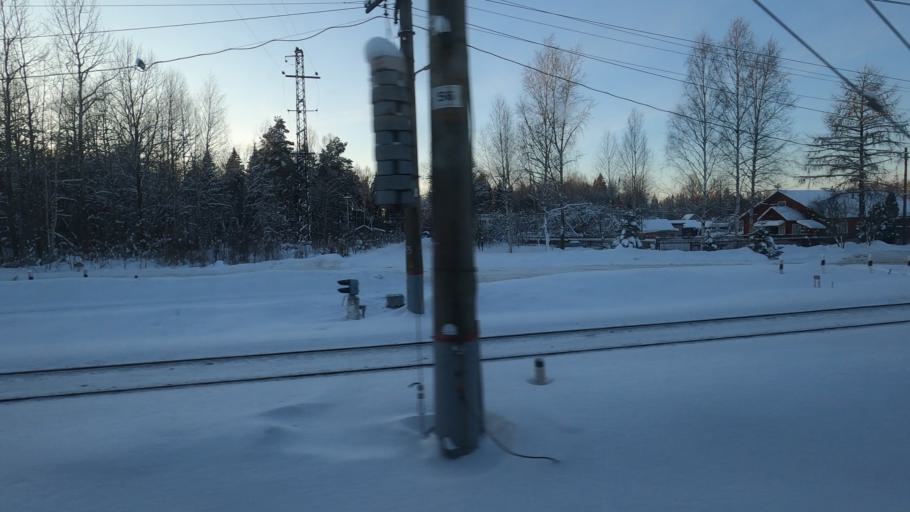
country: RU
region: Moskovskaya
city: Novo-Nikol'skoye
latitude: 56.5430
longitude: 37.5599
